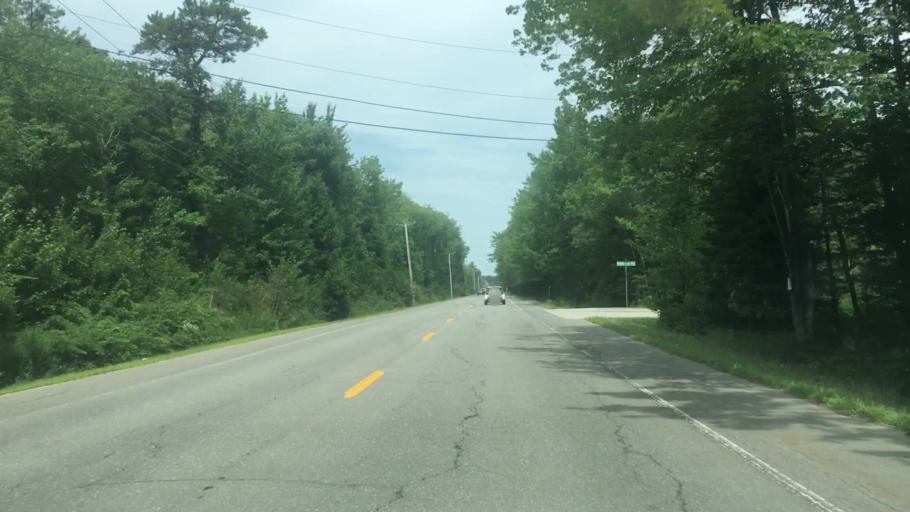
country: US
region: Maine
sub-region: Cumberland County
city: Scarborough
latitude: 43.5960
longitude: -70.2914
